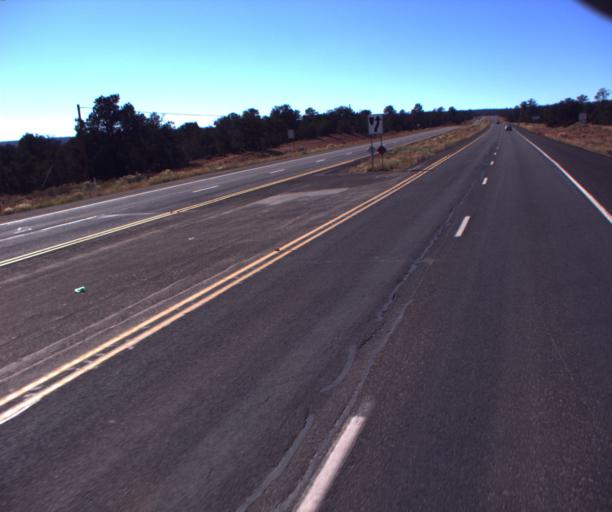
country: US
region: Arizona
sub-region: Apache County
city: Saint Michaels
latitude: 35.6595
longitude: -109.1239
